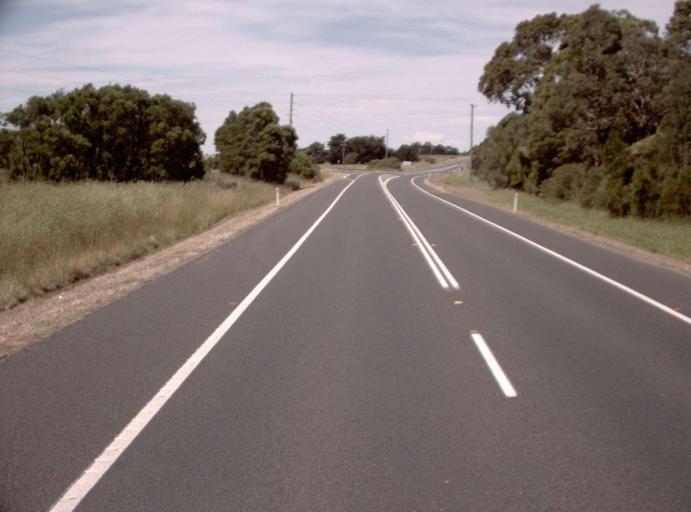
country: AU
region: Victoria
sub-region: Wellington
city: Heyfield
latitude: -38.1082
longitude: 146.8951
